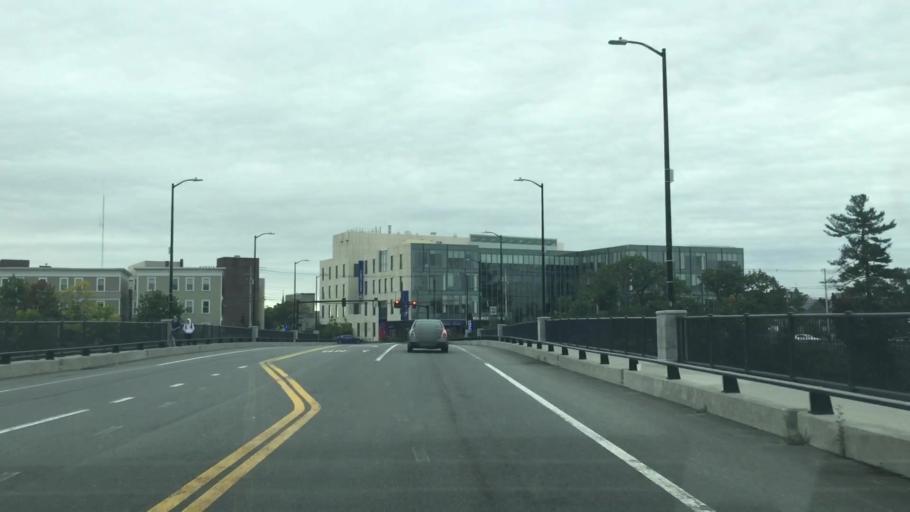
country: US
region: Massachusetts
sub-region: Middlesex County
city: Lowell
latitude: 42.6518
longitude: -71.3249
